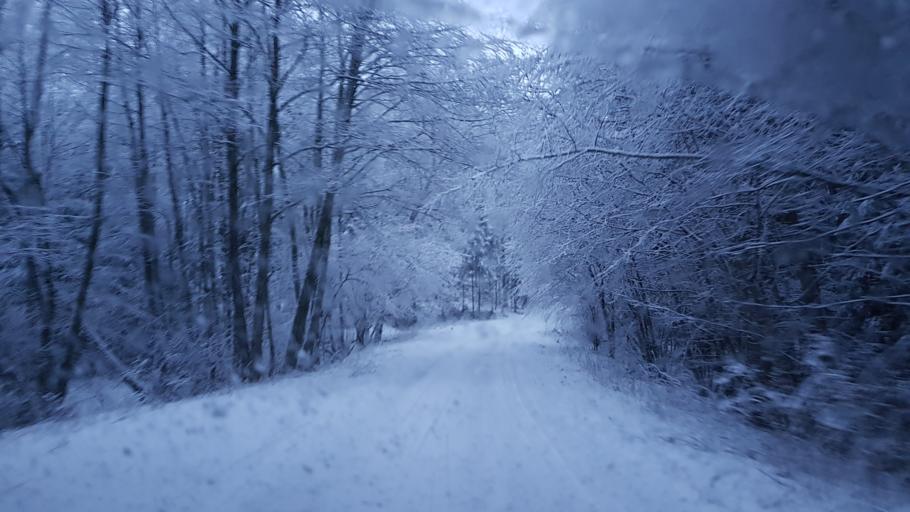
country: PL
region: West Pomeranian Voivodeship
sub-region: Powiat koszalinski
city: Sianow
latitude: 54.1664
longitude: 16.4737
